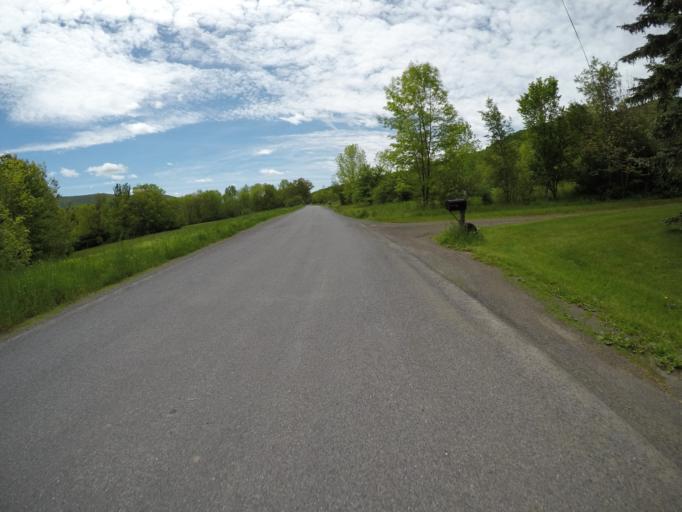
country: US
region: New York
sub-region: Delaware County
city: Stamford
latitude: 42.2816
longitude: -74.5160
